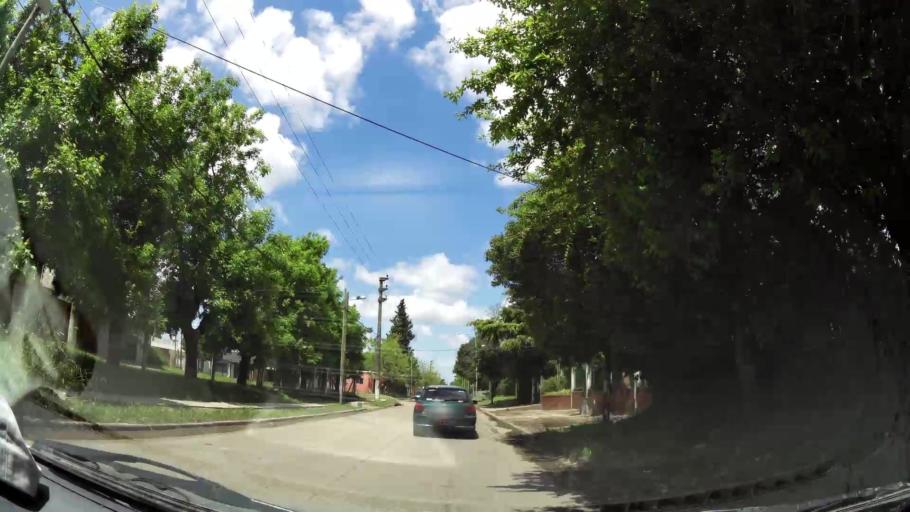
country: AR
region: Buenos Aires
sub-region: Partido de Quilmes
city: Quilmes
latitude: -34.8224
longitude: -58.2491
